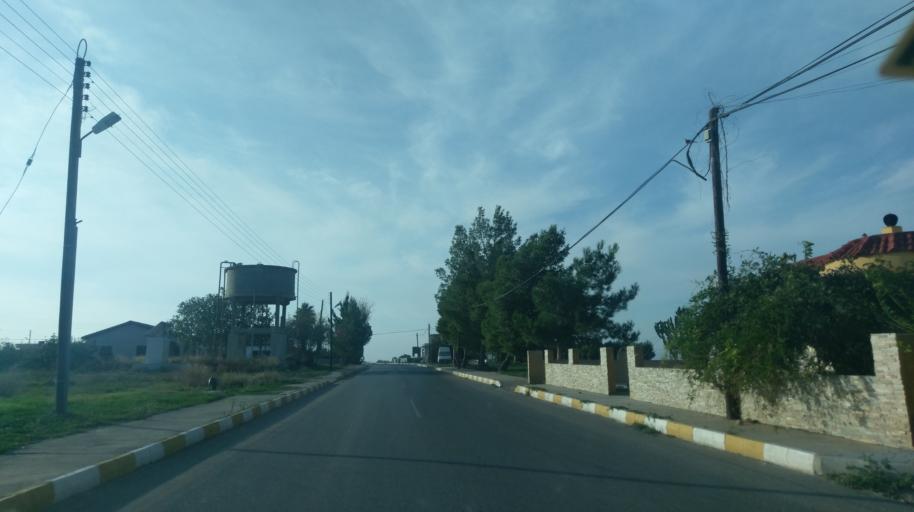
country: CY
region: Ammochostos
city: Achna
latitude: 35.1088
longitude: 33.7489
